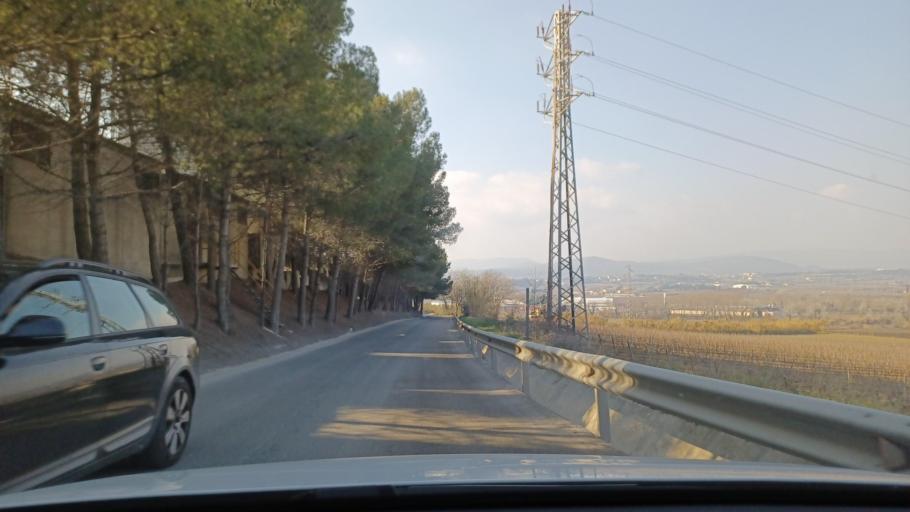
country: ES
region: Catalonia
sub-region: Provincia de Barcelona
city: Vilafranca del Penedes
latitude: 41.3657
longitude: 1.6847
